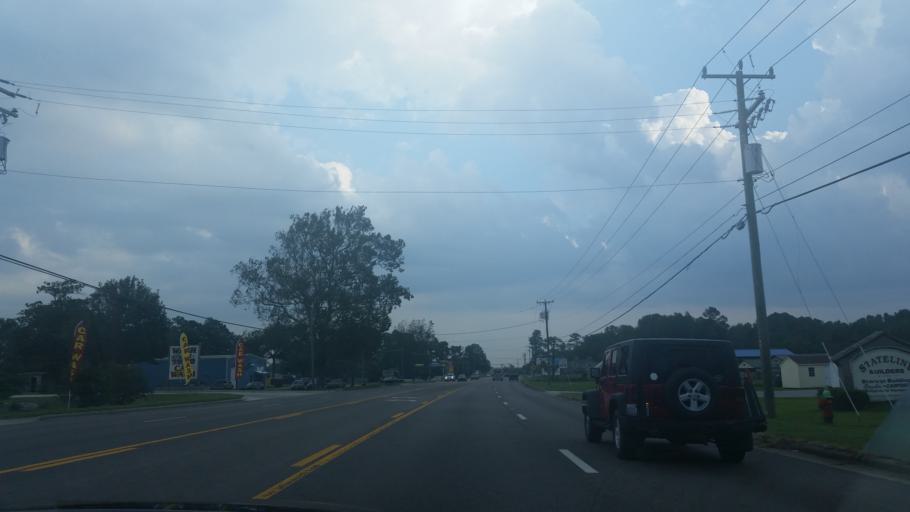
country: US
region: North Carolina
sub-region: Dare County
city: Southern Shores
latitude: 36.2349
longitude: -75.8742
